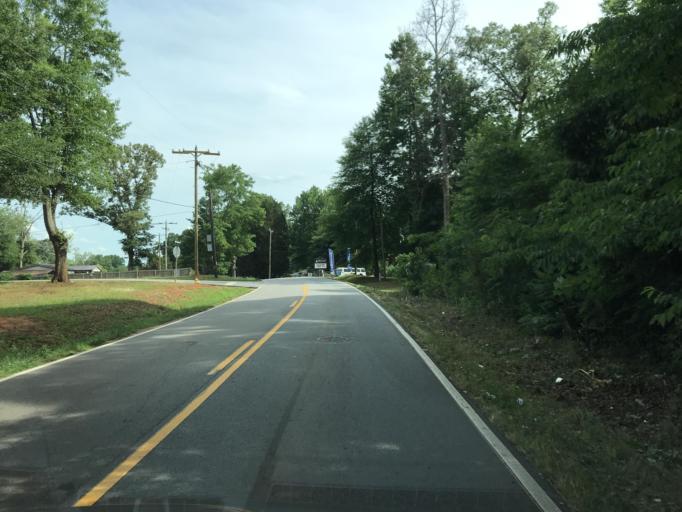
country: US
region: South Carolina
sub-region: Greenville County
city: Gantt
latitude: 34.7712
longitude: -82.4166
